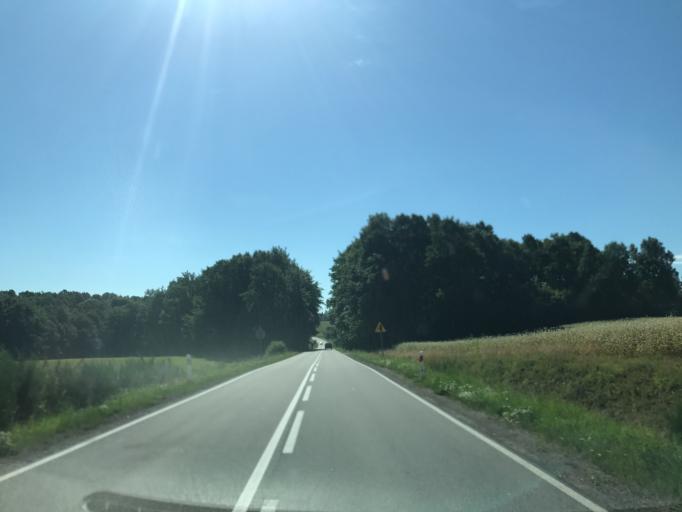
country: PL
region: Pomeranian Voivodeship
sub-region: Powiat leborski
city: Cewice
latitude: 54.3376
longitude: 17.7058
